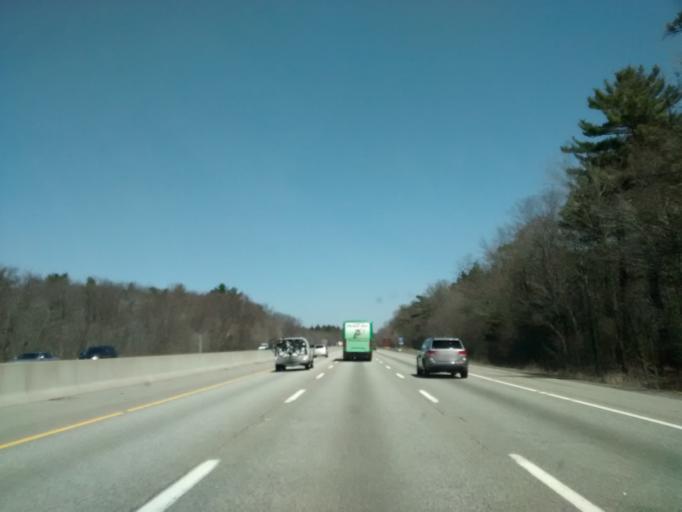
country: US
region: Massachusetts
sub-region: Worcester County
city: Westborough
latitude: 42.2550
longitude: -71.5815
